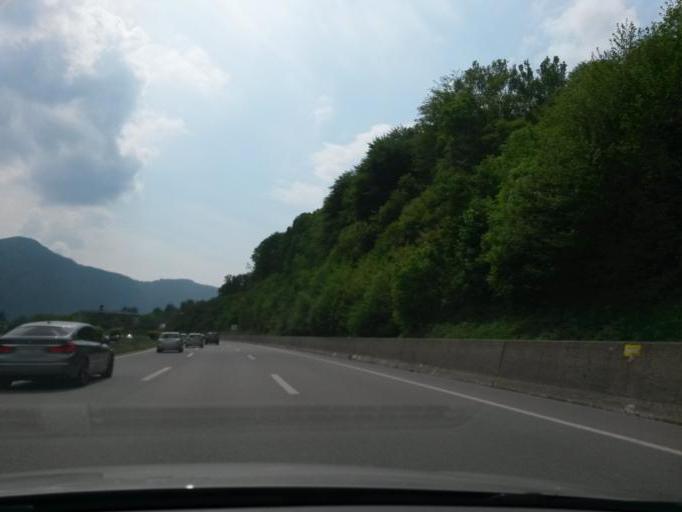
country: CH
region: Ticino
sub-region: Bellinzona District
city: Cadenazzo
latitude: 46.1270
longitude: 8.9181
